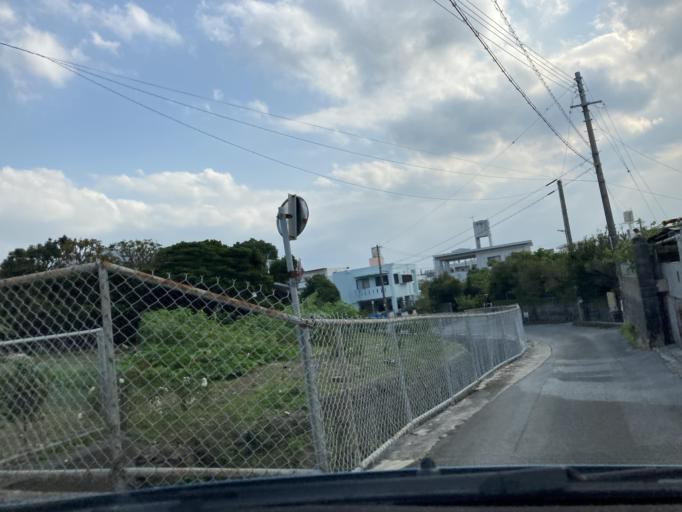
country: JP
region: Okinawa
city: Tomigusuku
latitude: 26.1879
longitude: 127.7264
